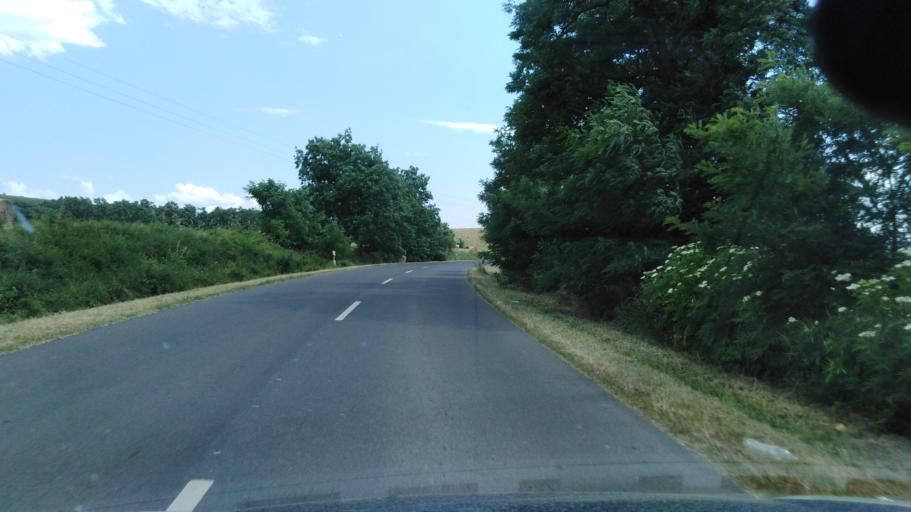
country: HU
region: Nograd
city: Szecseny
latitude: 48.1668
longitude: 19.5363
